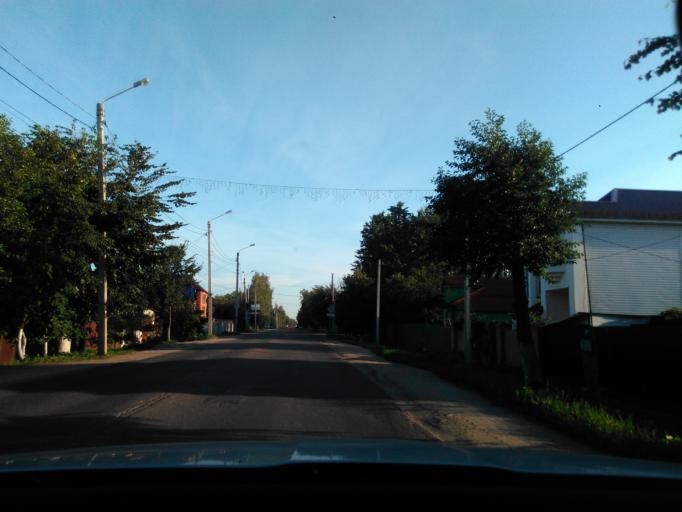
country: RU
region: Tverskaya
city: Konakovo
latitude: 56.7028
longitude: 36.7683
